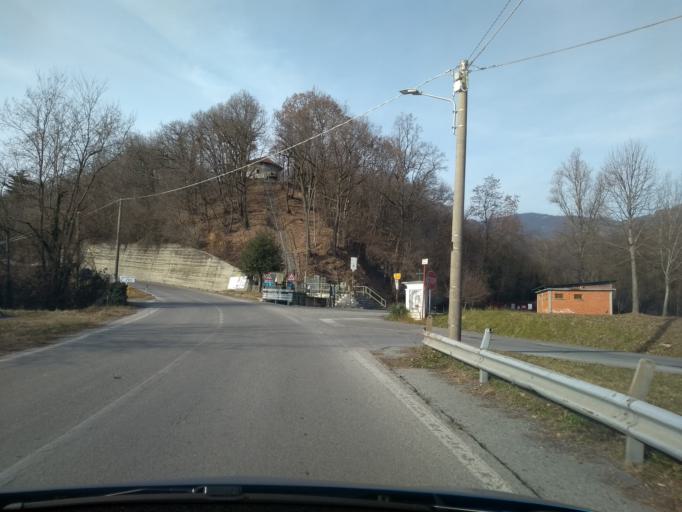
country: IT
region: Piedmont
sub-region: Provincia di Torino
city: Balangero
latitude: 45.2772
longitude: 7.5121
